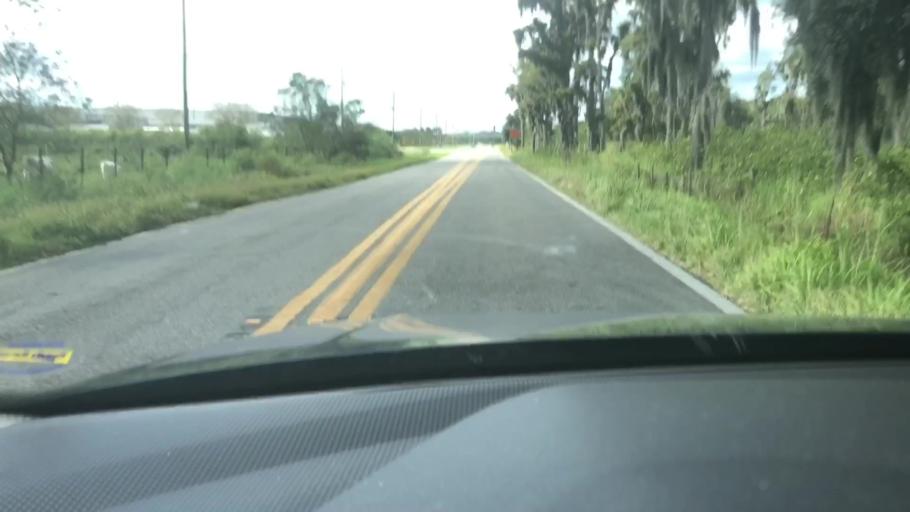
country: US
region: Florida
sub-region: Polk County
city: Winston
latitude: 28.0296
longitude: -82.0314
